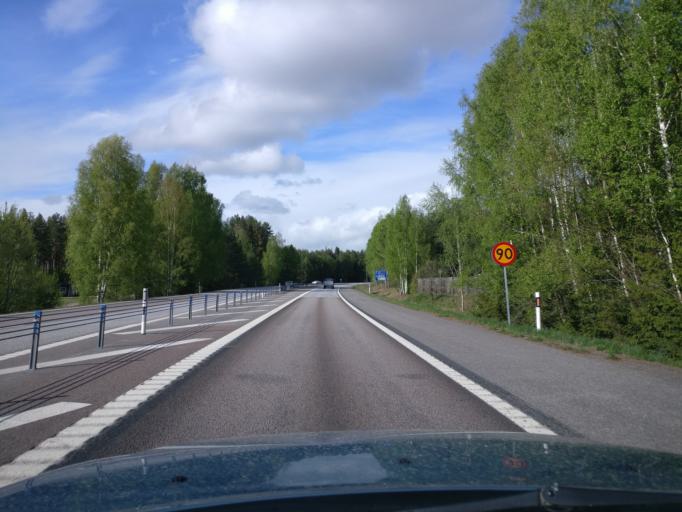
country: SE
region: Vaermland
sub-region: Forshaga Kommun
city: Forshaga
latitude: 59.4803
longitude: 13.4115
